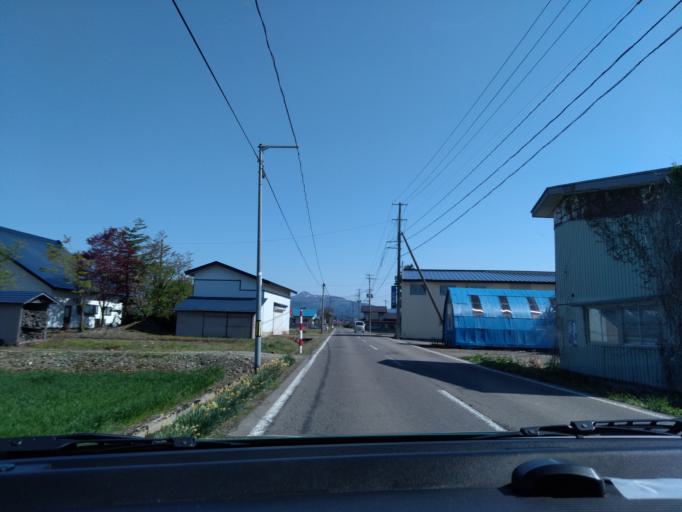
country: JP
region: Akita
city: Kakunodatemachi
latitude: 39.5170
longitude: 140.5897
